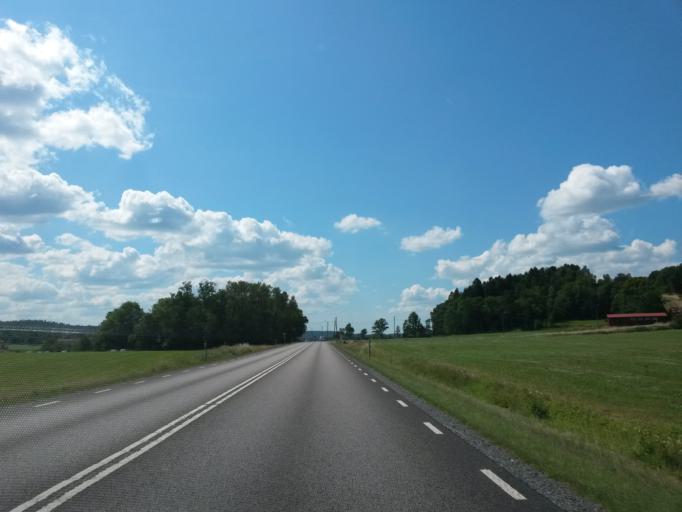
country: SE
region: Vaestra Goetaland
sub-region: Lerums Kommun
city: Olstorp
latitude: 57.8125
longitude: 12.1792
